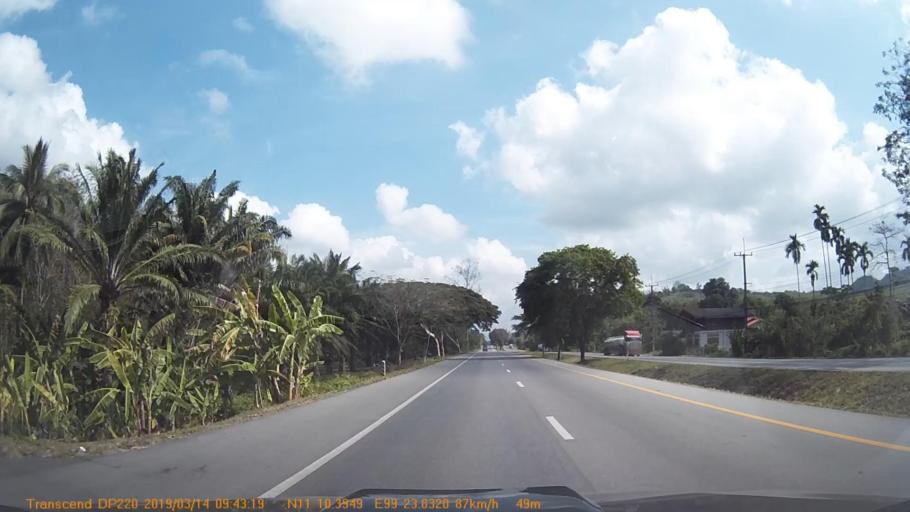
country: TH
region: Prachuap Khiri Khan
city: Bang Saphan Noi
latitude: 11.1734
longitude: 99.3972
